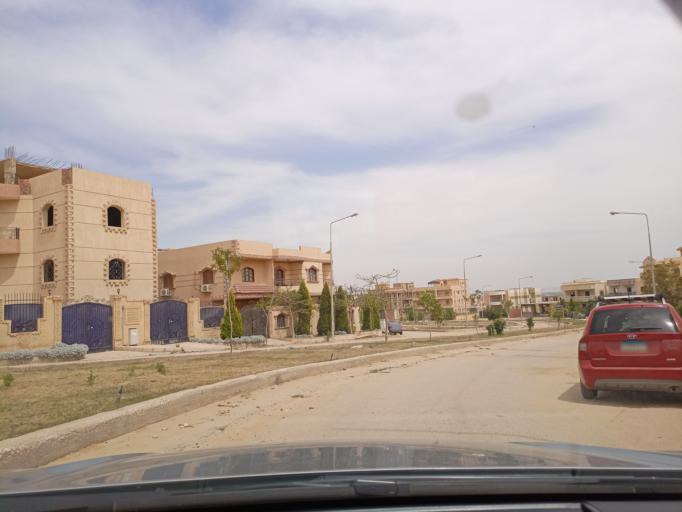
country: EG
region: Muhafazat al Qalyubiyah
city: Al Khankah
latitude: 30.2386
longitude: 31.4883
